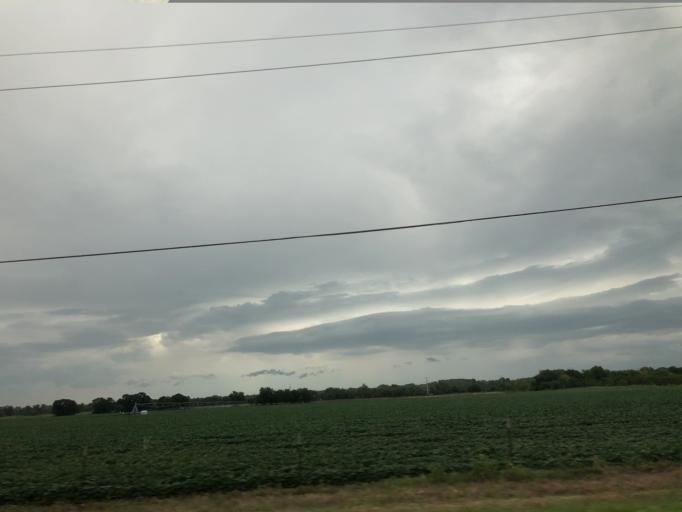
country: US
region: Kansas
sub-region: Reno County
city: Hutchinson
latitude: 38.1147
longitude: -97.9520
